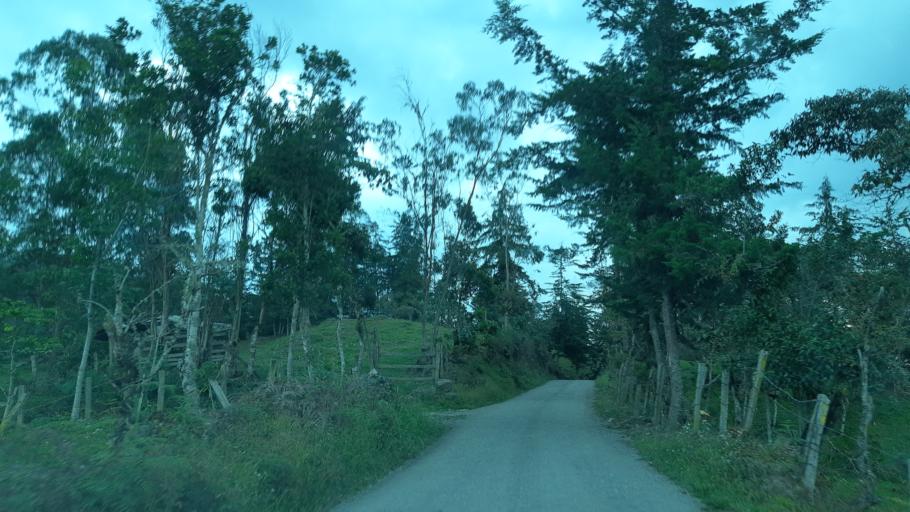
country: CO
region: Boyaca
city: Garagoa
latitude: 5.1166
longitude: -73.3491
